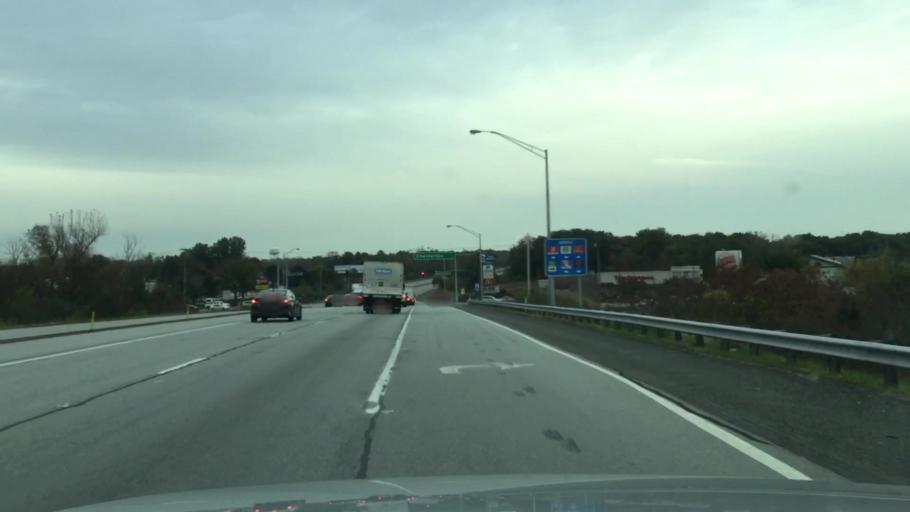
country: US
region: Indiana
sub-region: Porter County
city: Chesterton
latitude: 41.6186
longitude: -87.0427
